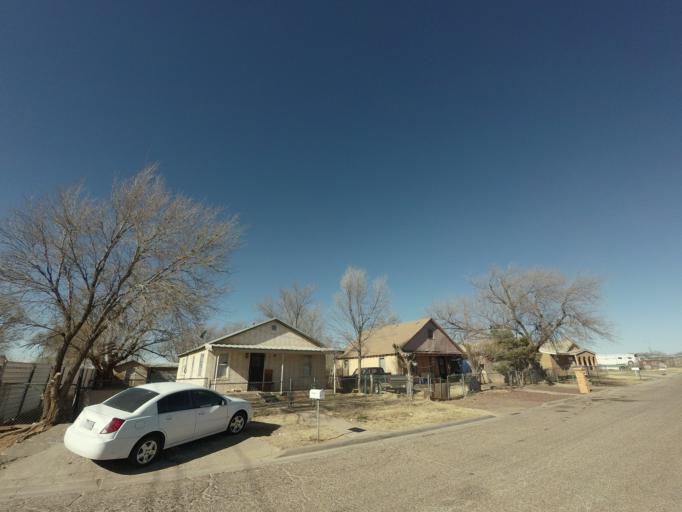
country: US
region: New Mexico
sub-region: Curry County
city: Clovis
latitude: 34.4013
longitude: -103.2343
